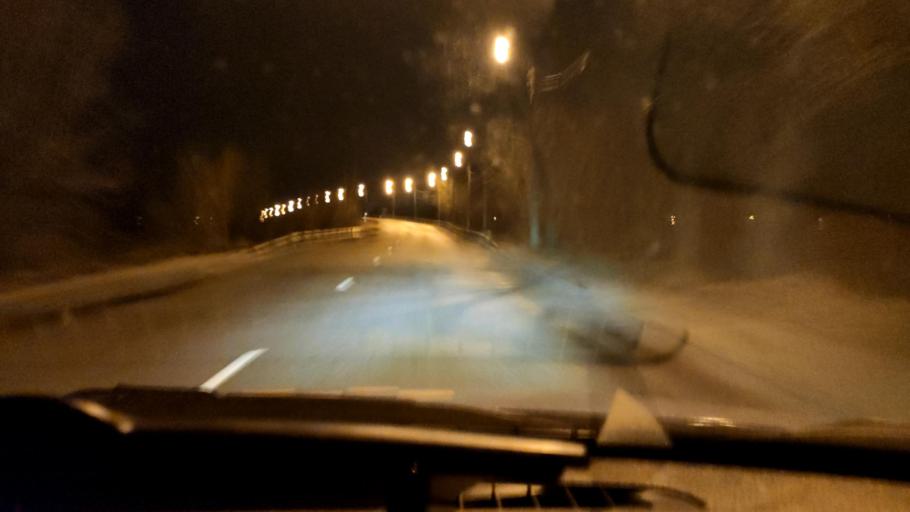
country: RU
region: Voronezj
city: Somovo
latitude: 51.7439
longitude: 39.3408
